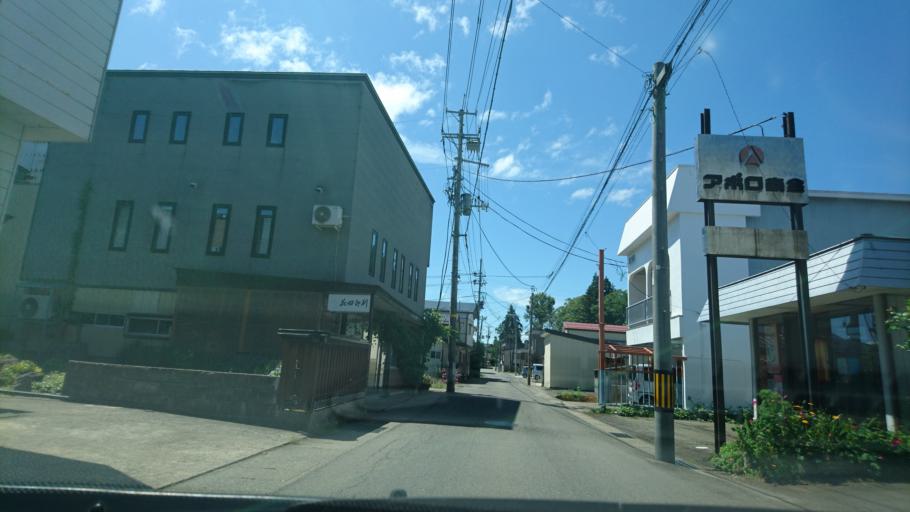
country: JP
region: Akita
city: Kakunodatemachi
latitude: 39.5894
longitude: 140.5642
